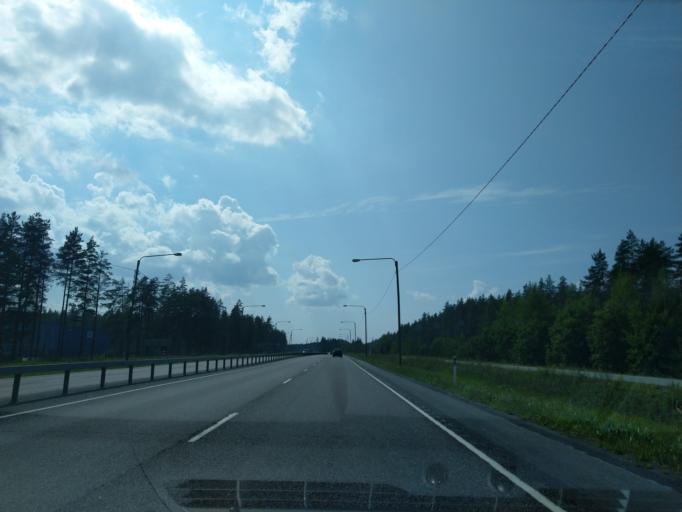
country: FI
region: South Karelia
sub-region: Lappeenranta
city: Joutseno
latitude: 61.0978
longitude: 28.3842
